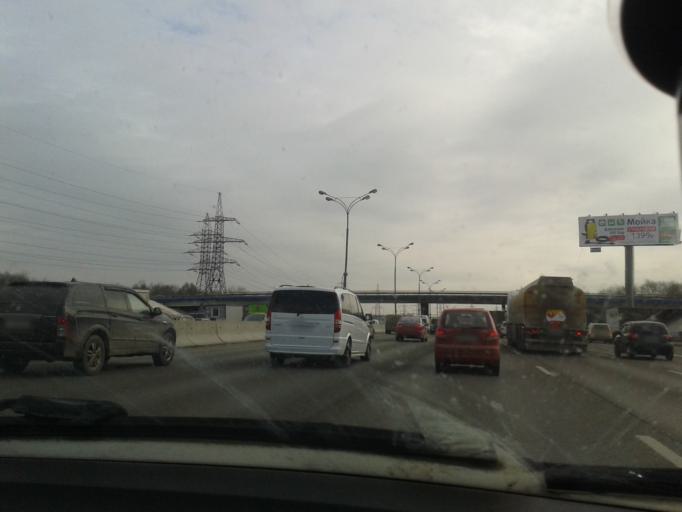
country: RU
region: Moscow
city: Vagonoremont
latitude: 55.9096
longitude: 37.5614
